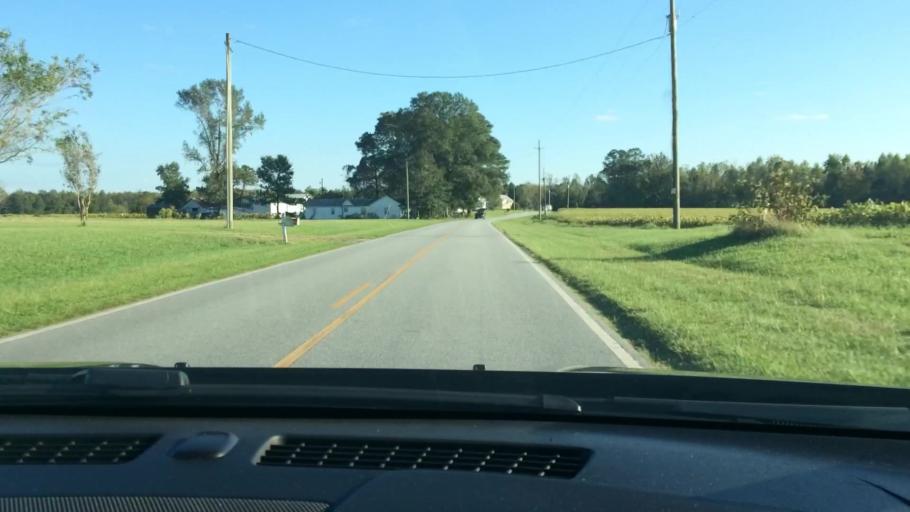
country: US
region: North Carolina
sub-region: Pitt County
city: Winterville
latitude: 35.5186
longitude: -77.4325
